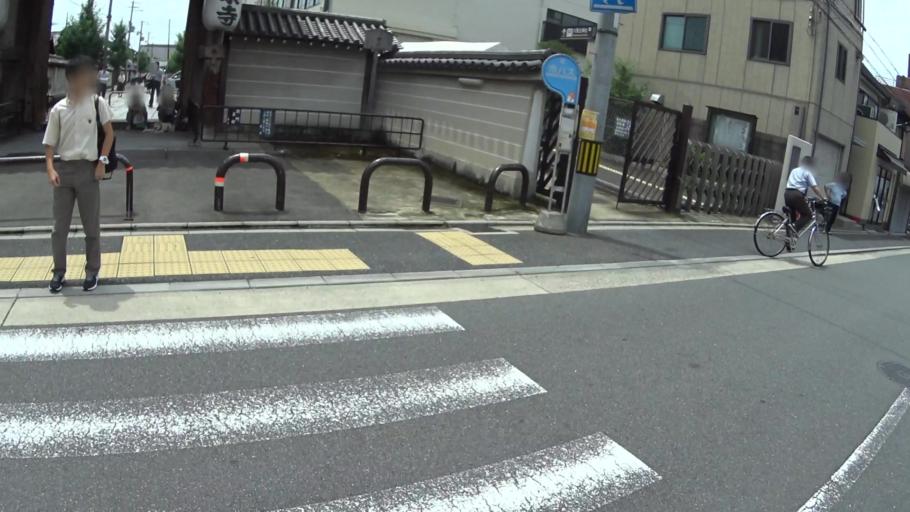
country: JP
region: Kyoto
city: Kyoto
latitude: 34.9843
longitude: 135.7477
